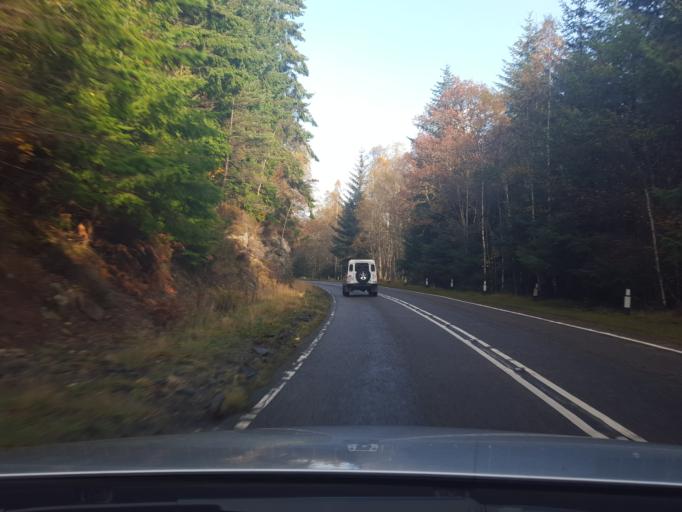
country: GB
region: Scotland
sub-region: Highland
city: Beauly
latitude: 57.2030
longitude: -4.7025
